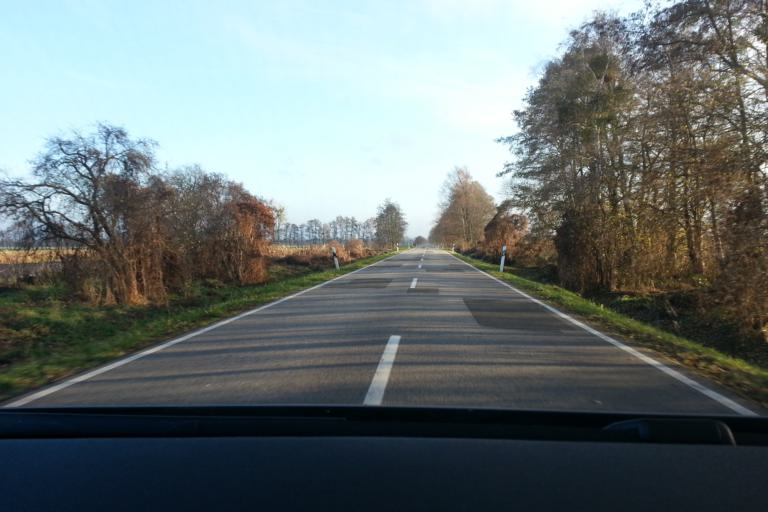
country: DE
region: Mecklenburg-Vorpommern
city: Ducherow
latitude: 53.6432
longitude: 13.7408
